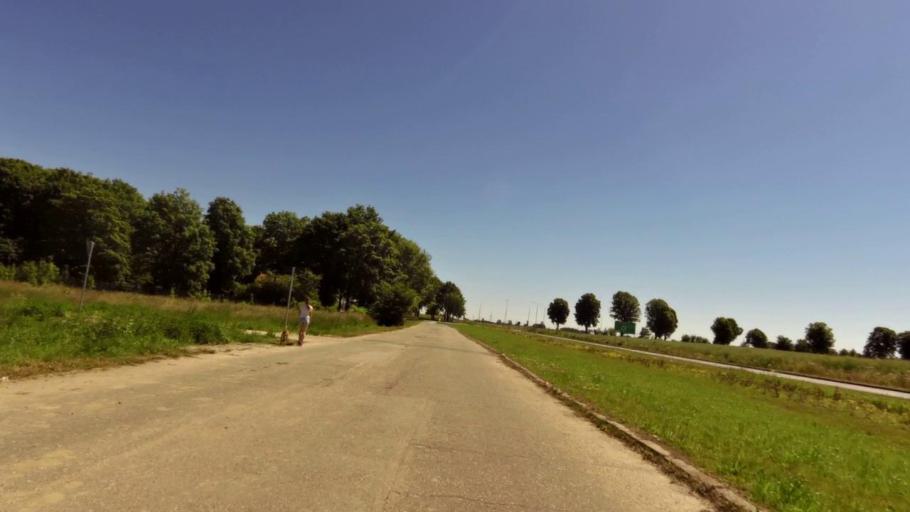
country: PL
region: West Pomeranian Voivodeship
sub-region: Powiat kolobrzeski
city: Goscino
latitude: 54.0474
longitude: 15.6496
